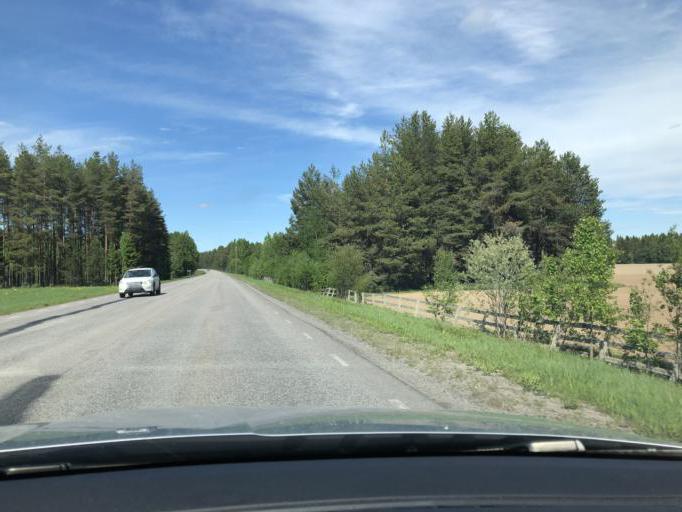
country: SE
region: Norrbotten
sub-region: Pitea Kommun
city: Bergsviken
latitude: 65.3576
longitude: 21.3789
